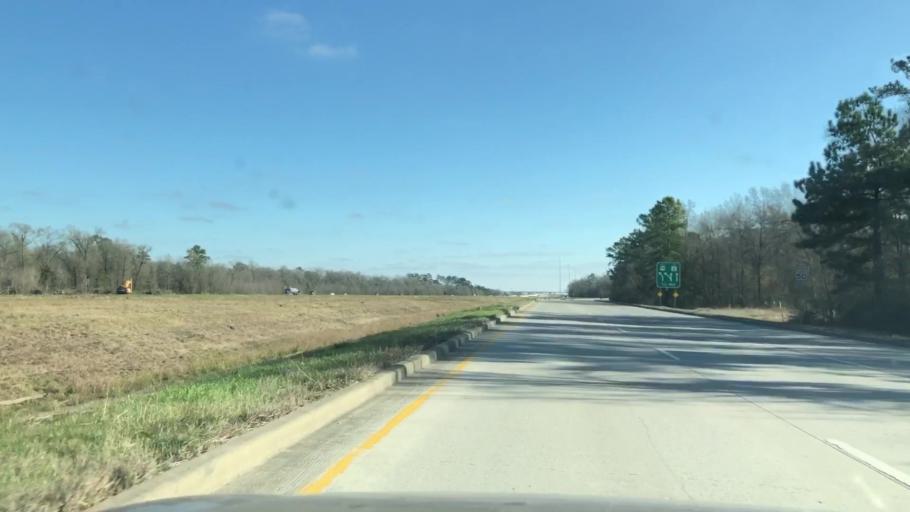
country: US
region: Texas
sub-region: Harris County
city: Cloverleaf
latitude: 29.8220
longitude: -95.1984
